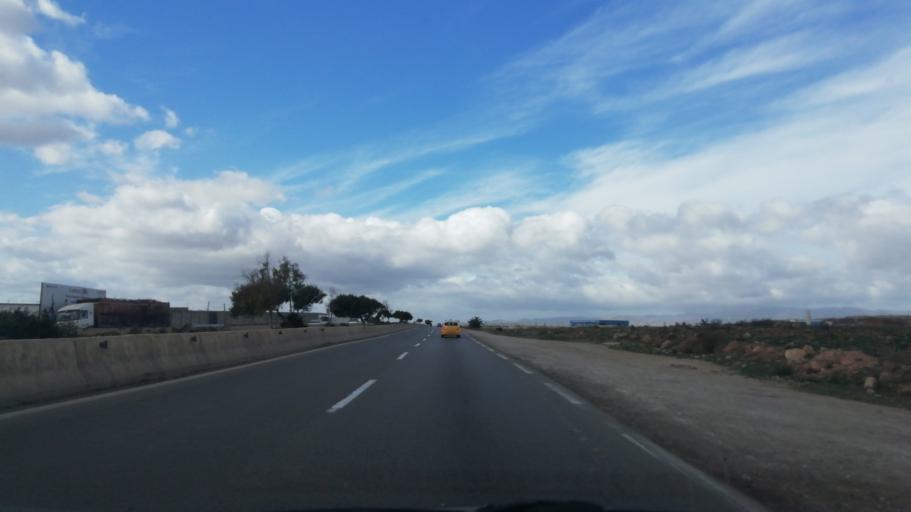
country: DZ
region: Oran
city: Ain el Bya
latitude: 35.7800
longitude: -0.2729
